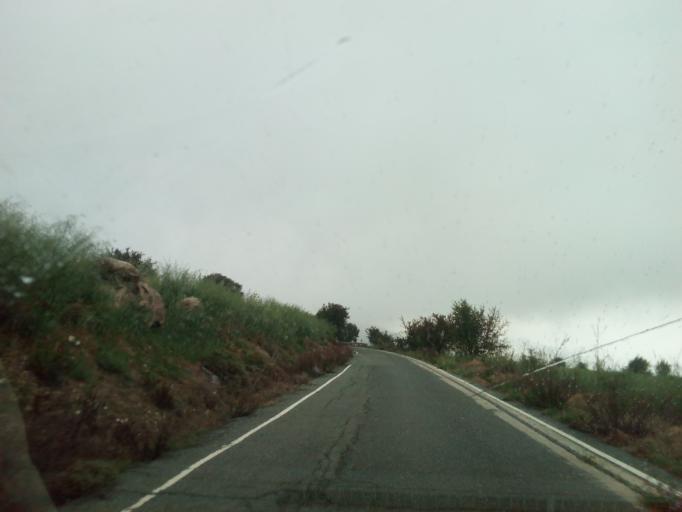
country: CY
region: Pafos
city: Mesogi
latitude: 34.8651
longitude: 32.6225
